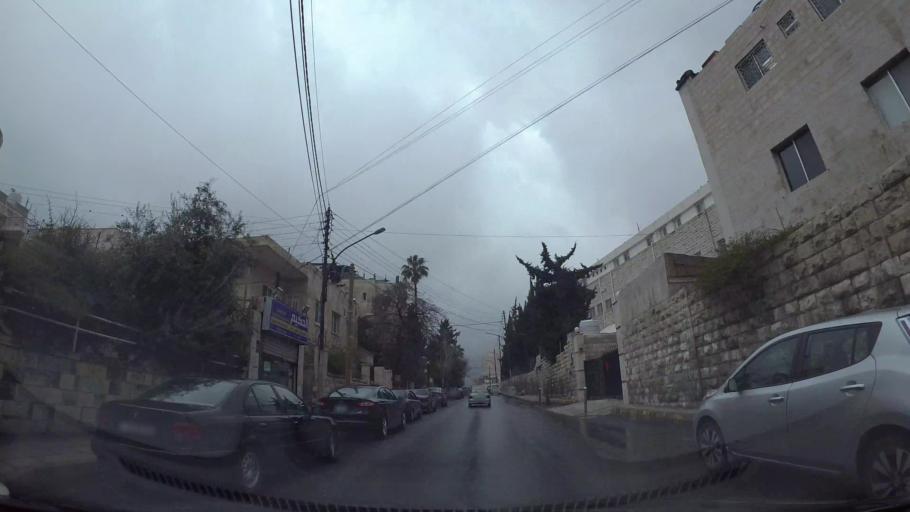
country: JO
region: Amman
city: Amman
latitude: 31.9493
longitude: 35.9189
